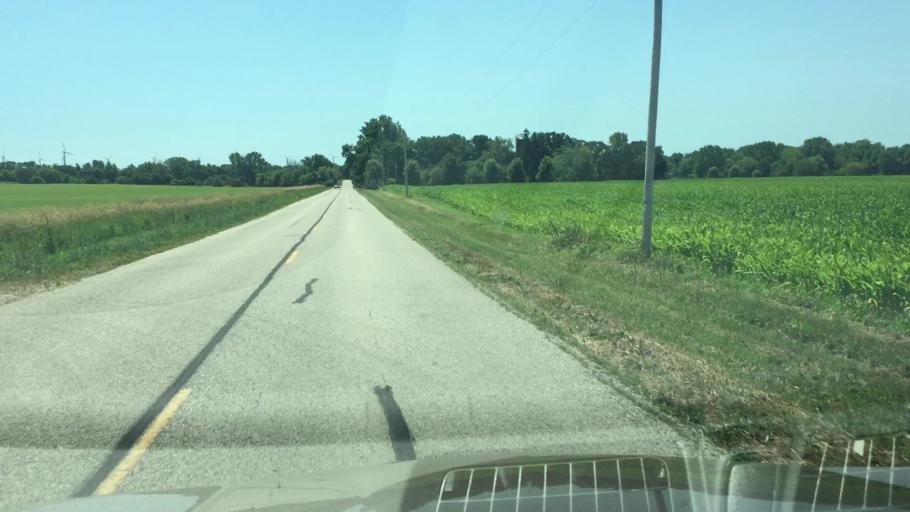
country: US
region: Wisconsin
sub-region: Fond du Lac County
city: Saint Peter
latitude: 43.9451
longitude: -88.3114
